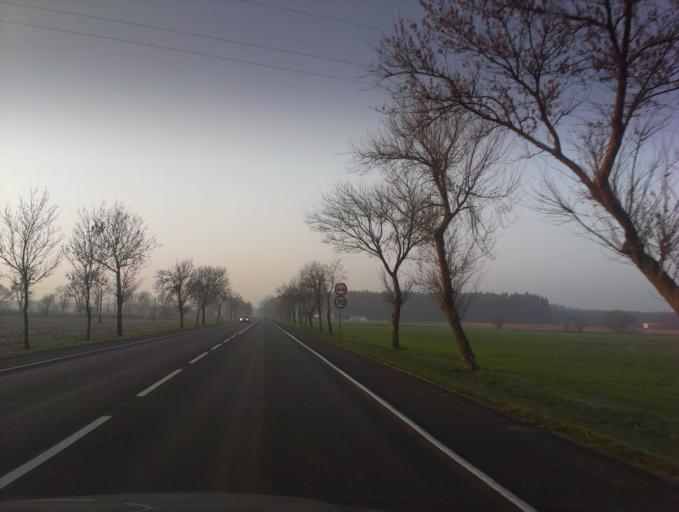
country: PL
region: Greater Poland Voivodeship
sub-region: Powiat obornicki
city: Rogozno
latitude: 52.7366
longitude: 16.9449
